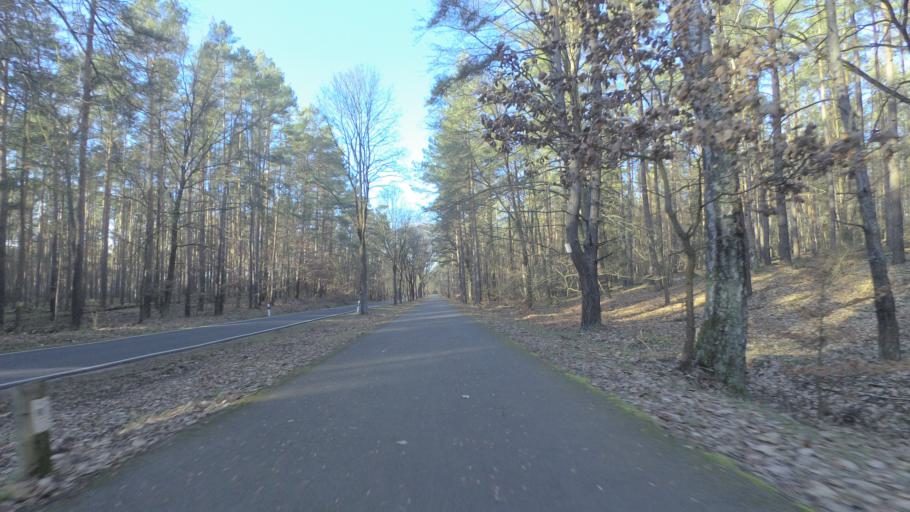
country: DE
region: Brandenburg
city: Ihlow
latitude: 52.0057
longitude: 13.3233
